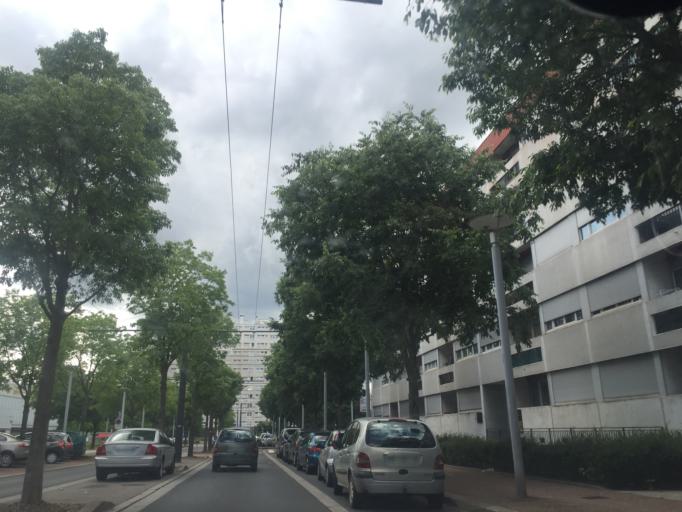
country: FR
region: Rhone-Alpes
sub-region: Departement du Rhone
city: Rillieux-la-Pape
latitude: 45.8150
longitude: 4.8959
